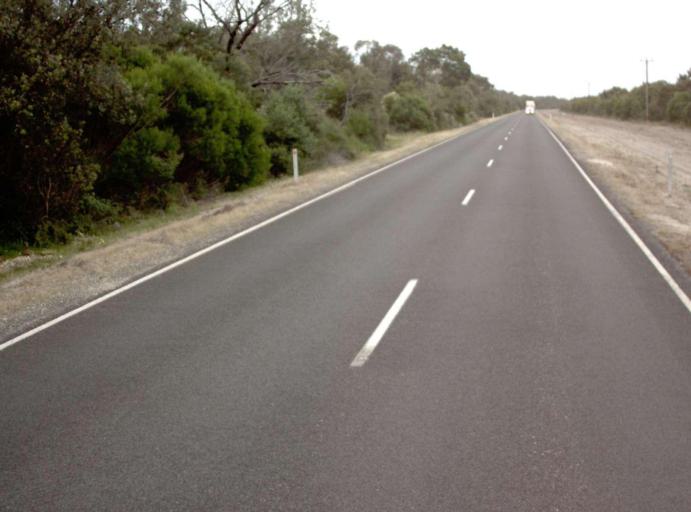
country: AU
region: Victoria
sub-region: East Gippsland
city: Bairnsdale
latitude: -38.0891
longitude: 147.5211
